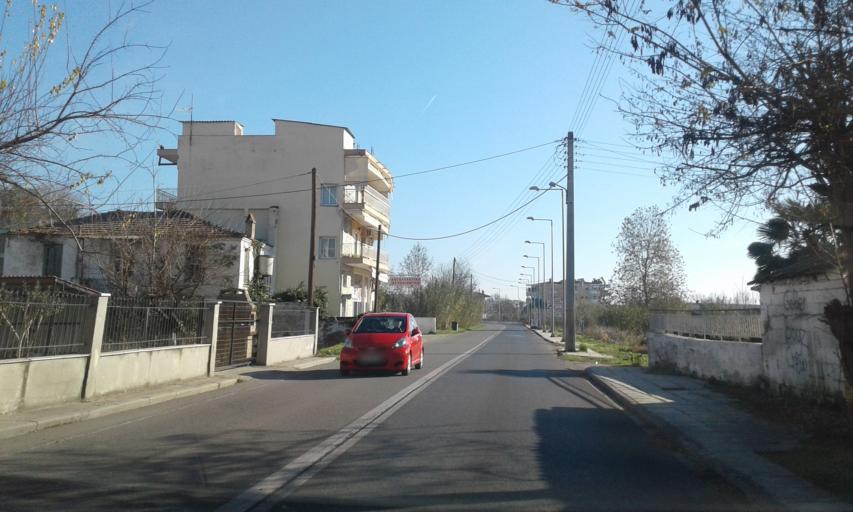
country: GR
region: Central Macedonia
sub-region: Nomos Thessalonikis
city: Lagkadas
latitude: 40.7460
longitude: 23.0664
